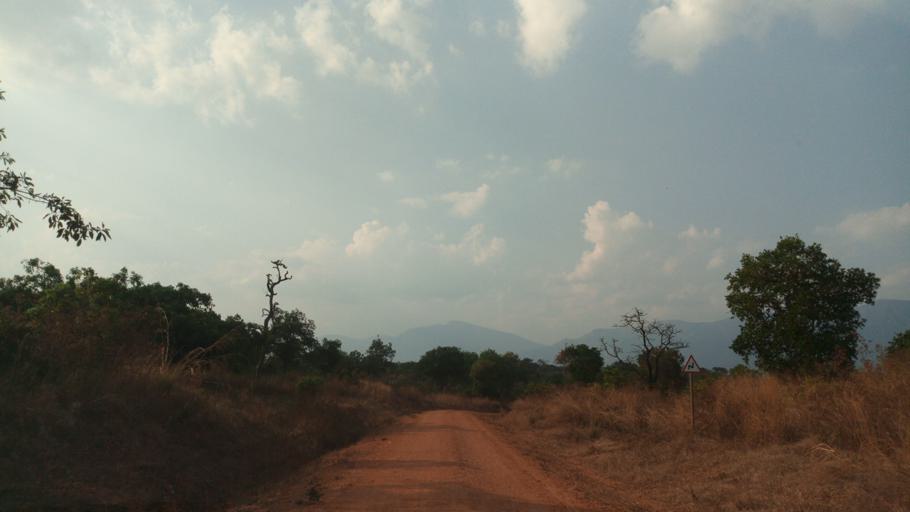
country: TZ
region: Kigoma
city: Kigoma
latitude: -5.1466
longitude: 28.9105
